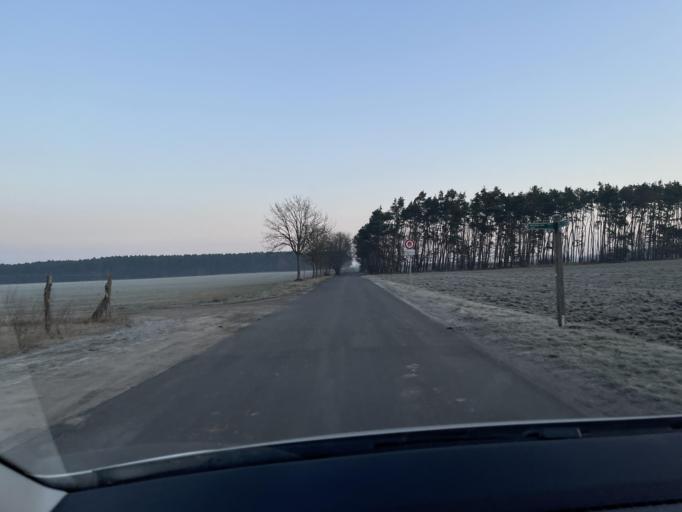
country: DE
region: Brandenburg
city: Roskow
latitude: 52.3945
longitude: 12.6922
